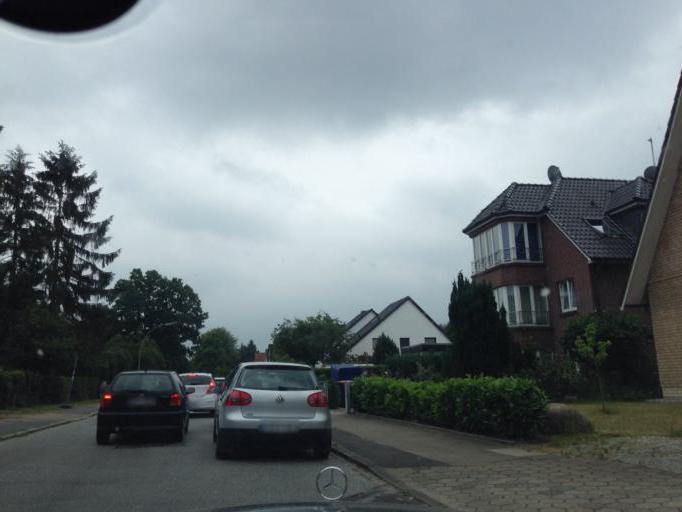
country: DE
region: Schleswig-Holstein
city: Barsbuettel
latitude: 53.5870
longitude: 10.1554
